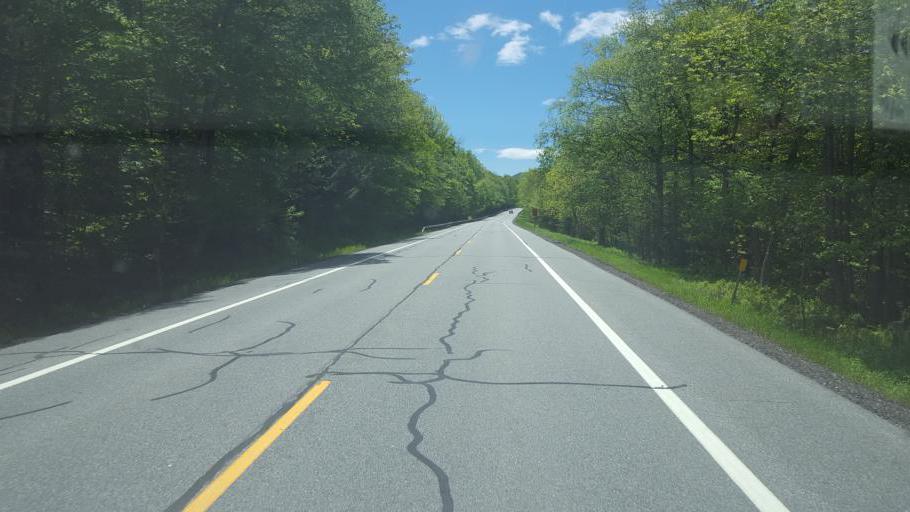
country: US
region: New York
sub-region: Hamilton County
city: Lake Pleasant
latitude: 43.6254
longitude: -74.4044
